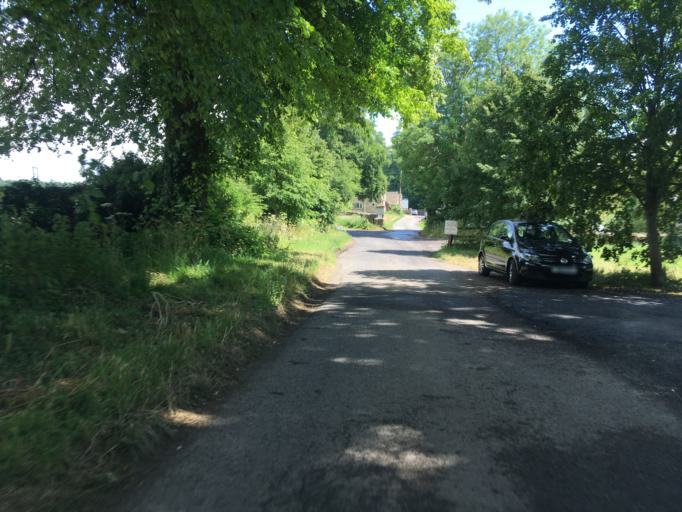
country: GB
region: England
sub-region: Gloucestershire
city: Tetbury
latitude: 51.6568
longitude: -2.1876
